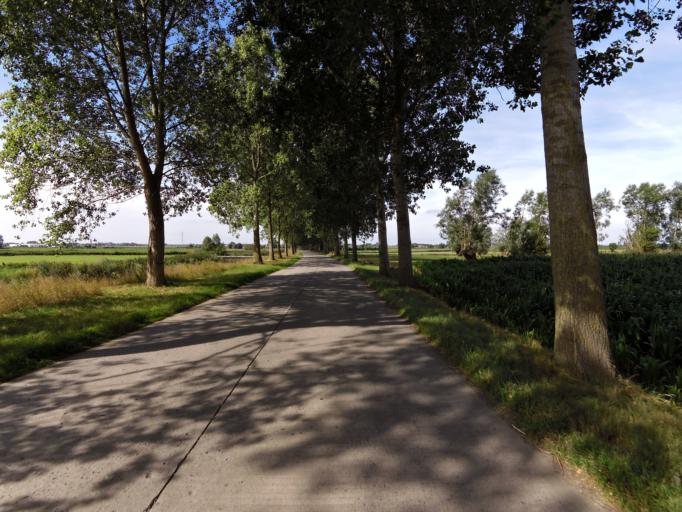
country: BE
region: Flanders
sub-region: Provincie West-Vlaanderen
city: Houthulst
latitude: 51.0272
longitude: 2.9522
